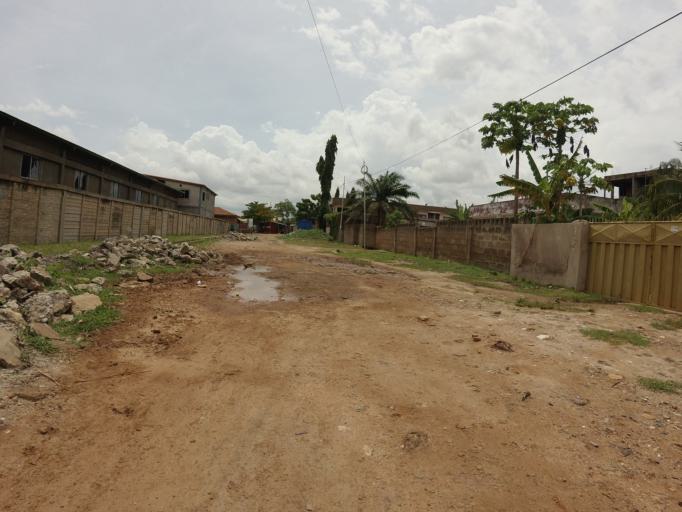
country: GH
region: Greater Accra
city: Accra
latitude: 5.6027
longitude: -0.2118
